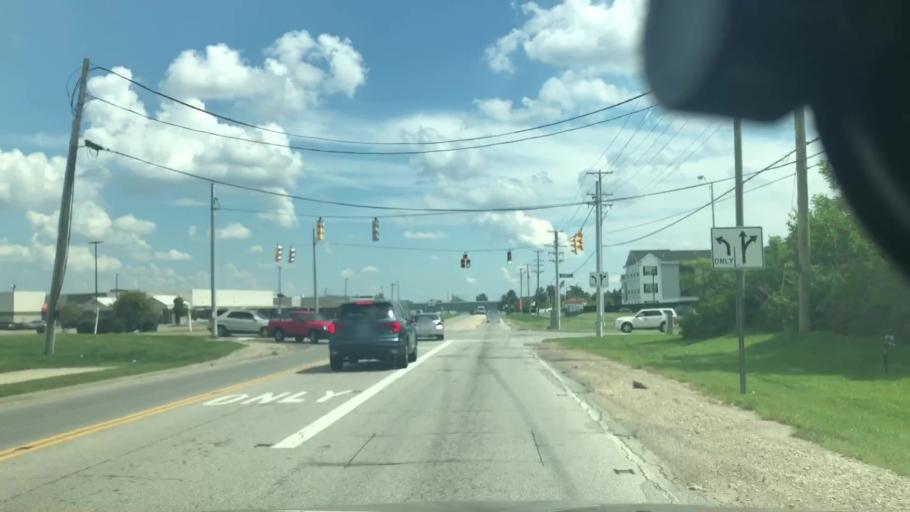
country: US
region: Ohio
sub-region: Franklin County
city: Lincoln Village
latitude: 39.9815
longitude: -83.1477
